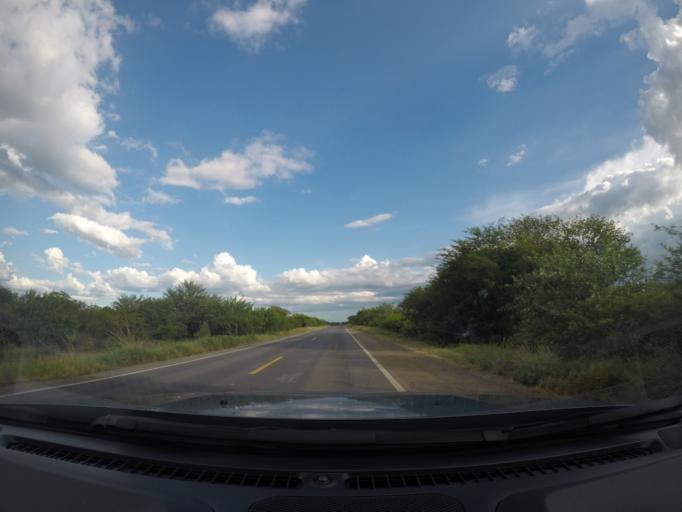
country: BR
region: Bahia
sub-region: Oliveira Dos Brejinhos
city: Beira Rio
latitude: -12.1917
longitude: -42.8226
